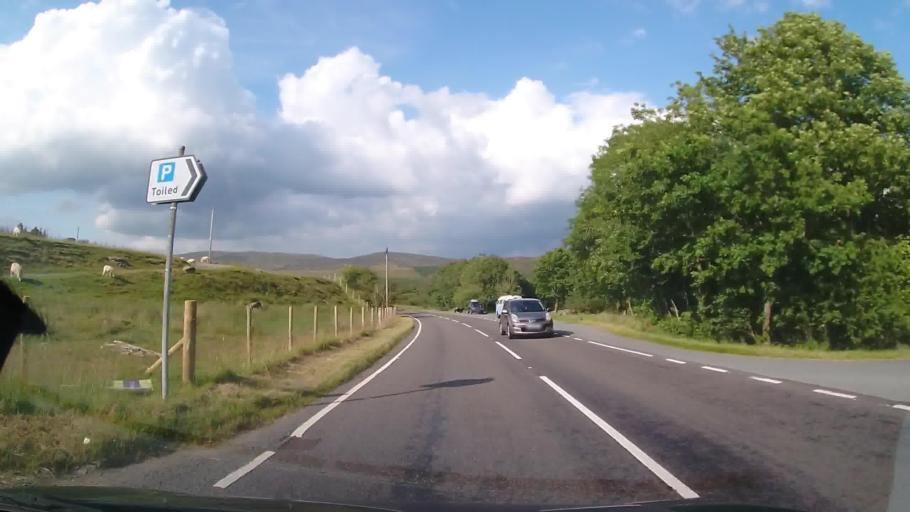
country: GB
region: Wales
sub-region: Gwynedd
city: Bala
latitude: 52.9479
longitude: -3.7208
